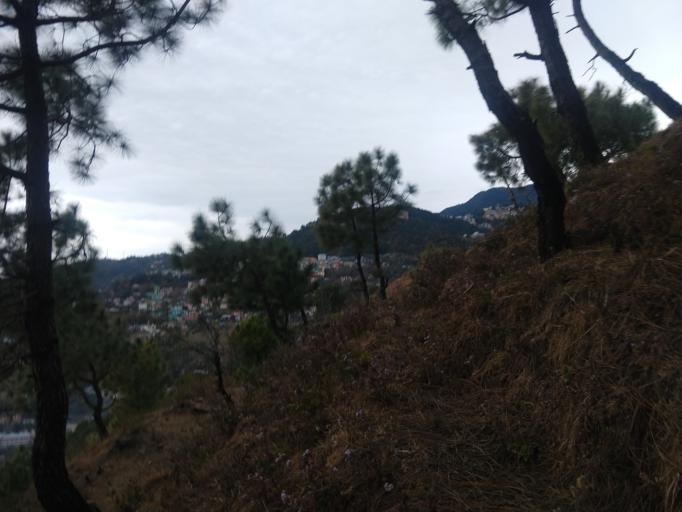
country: IN
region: Himachal Pradesh
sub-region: Kangra
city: Dharmsala
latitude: 32.2191
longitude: 76.3346
